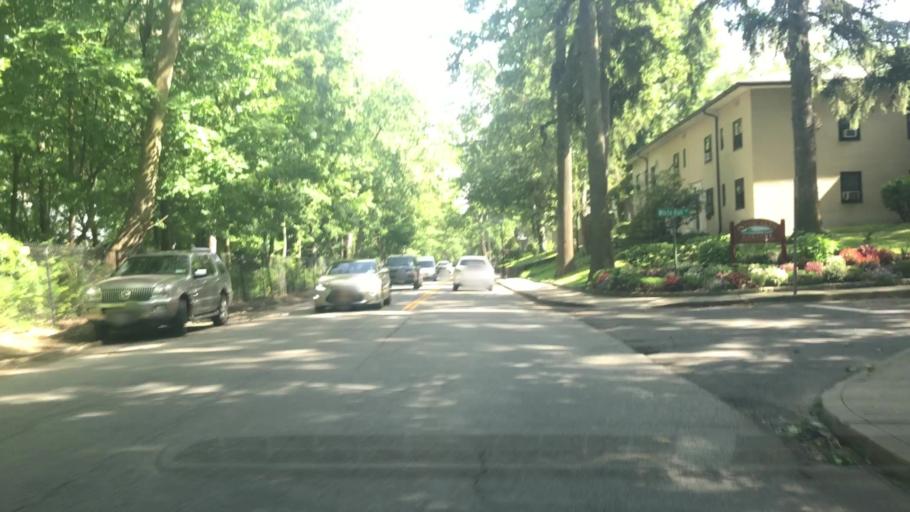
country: US
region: New York
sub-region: Westchester County
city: Tuckahoe
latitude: 40.9617
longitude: -73.8063
